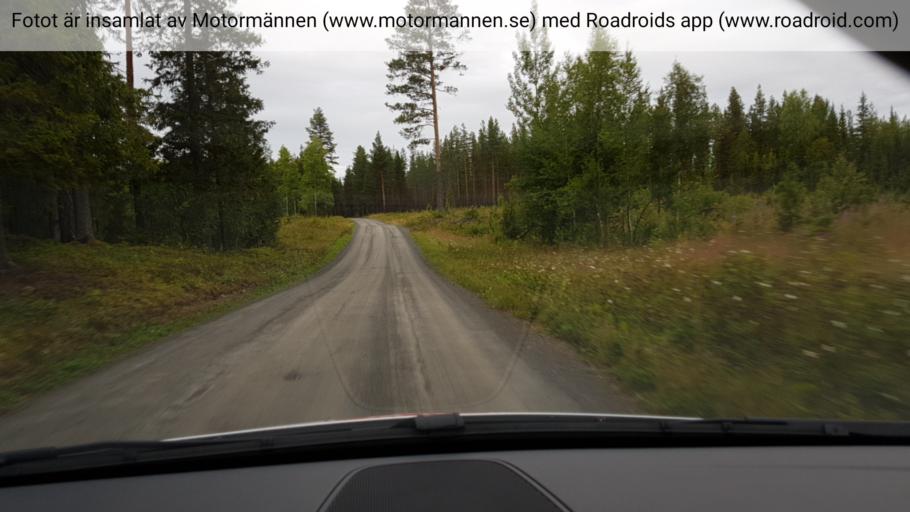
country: SE
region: Jaemtland
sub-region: OEstersunds Kommun
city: Lit
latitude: 63.5704
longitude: 14.7147
